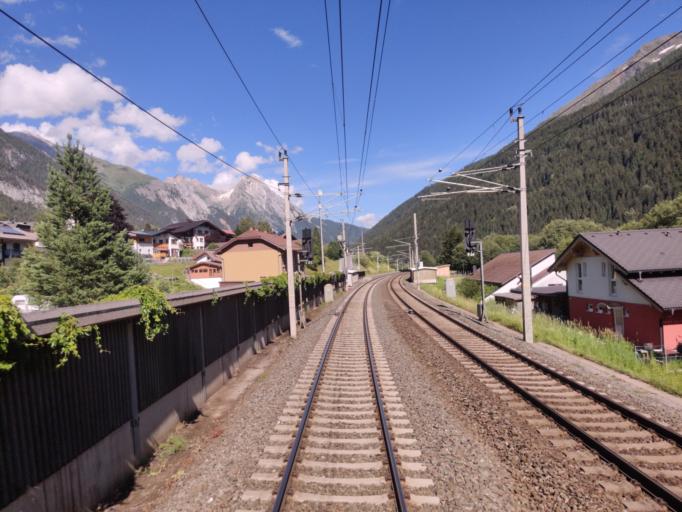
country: AT
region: Tyrol
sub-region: Politischer Bezirk Landeck
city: Flirsch
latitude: 47.1462
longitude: 10.3355
